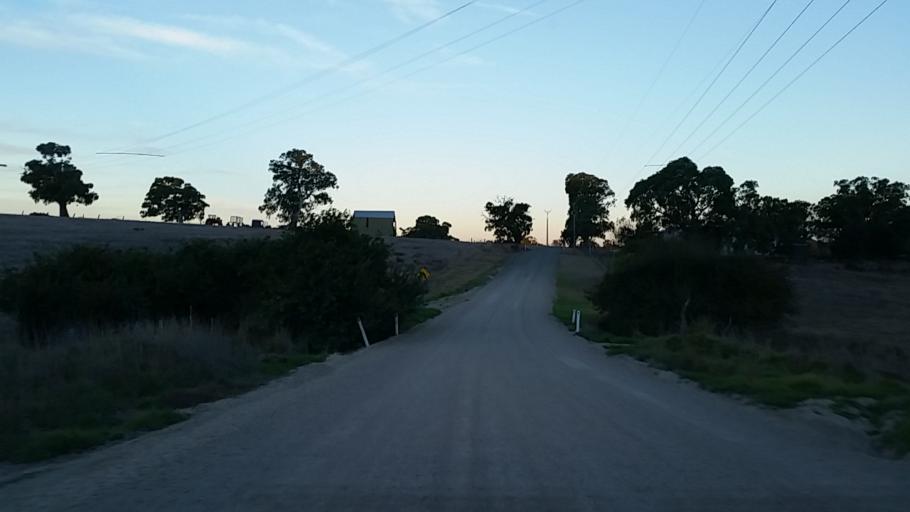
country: AU
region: South Australia
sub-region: Mount Barker
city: Nairne
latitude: -35.0813
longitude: 138.9269
